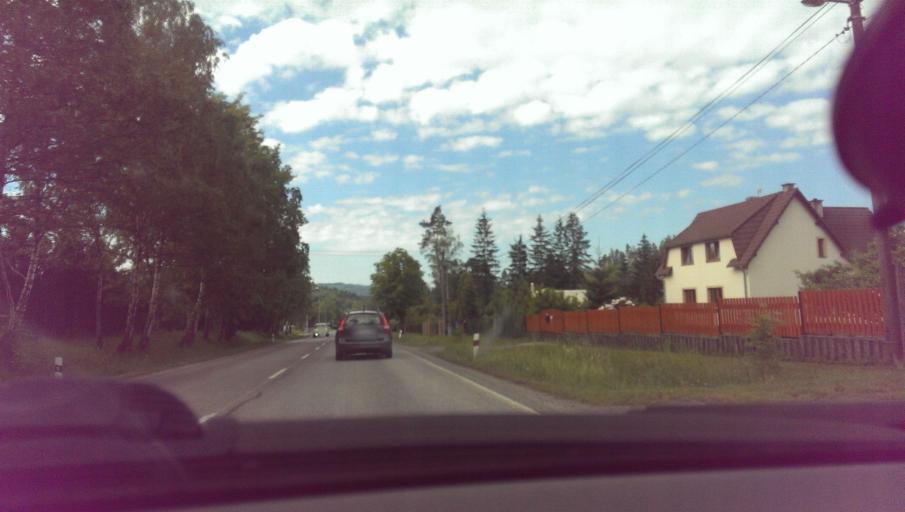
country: CZ
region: Zlin
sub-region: Okres Vsetin
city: Roznov pod Radhostem
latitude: 49.4750
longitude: 18.1635
